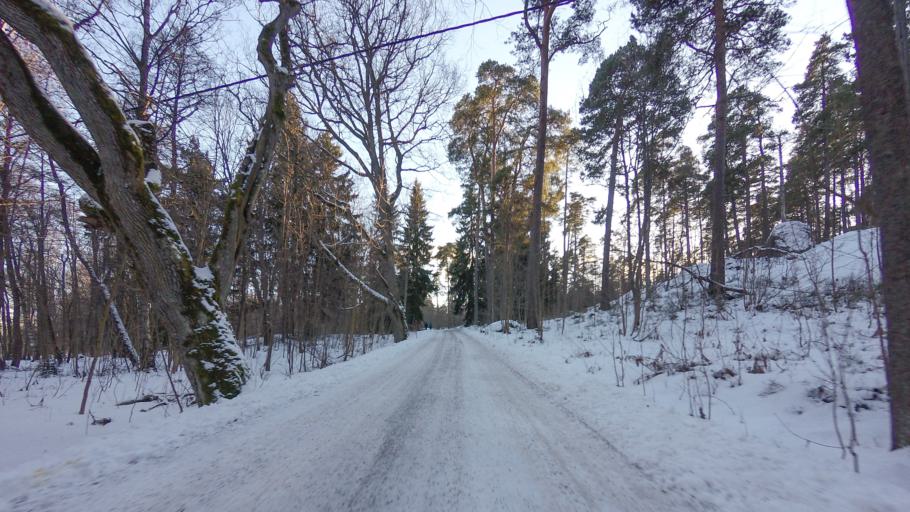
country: FI
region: Uusimaa
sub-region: Helsinki
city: Helsinki
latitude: 60.1672
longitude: 25.0275
